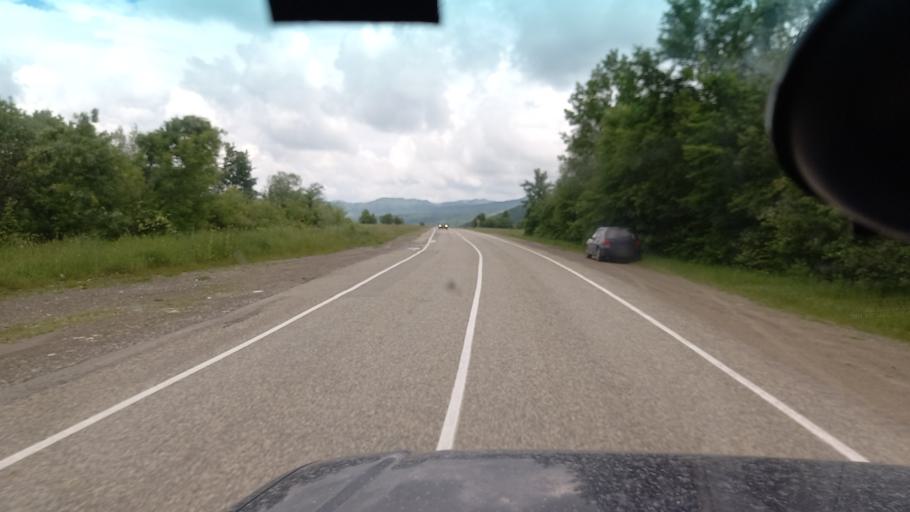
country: RU
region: Krasnodarskiy
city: Psebay
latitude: 44.0895
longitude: 40.7992
